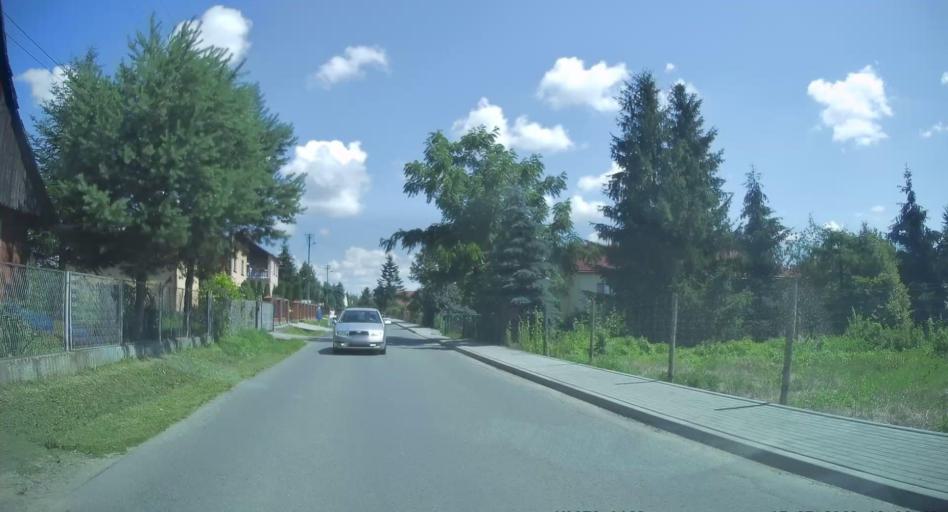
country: PL
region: Subcarpathian Voivodeship
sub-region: Powiat przemyski
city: Medyka
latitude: 49.8251
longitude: 22.8676
